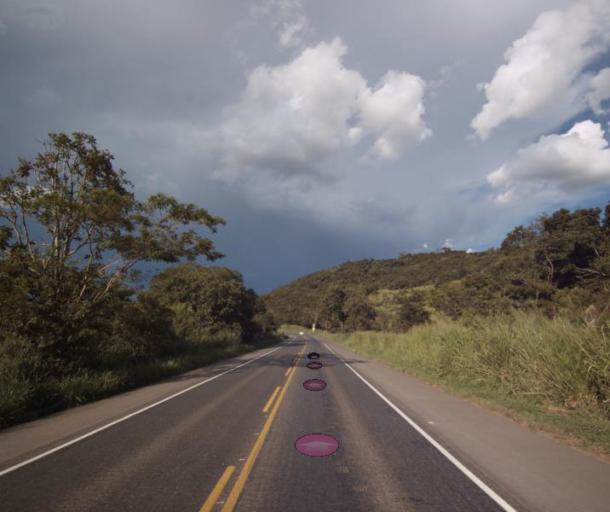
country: BR
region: Goias
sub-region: Rialma
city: Rialma
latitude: -15.2823
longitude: -49.5583
